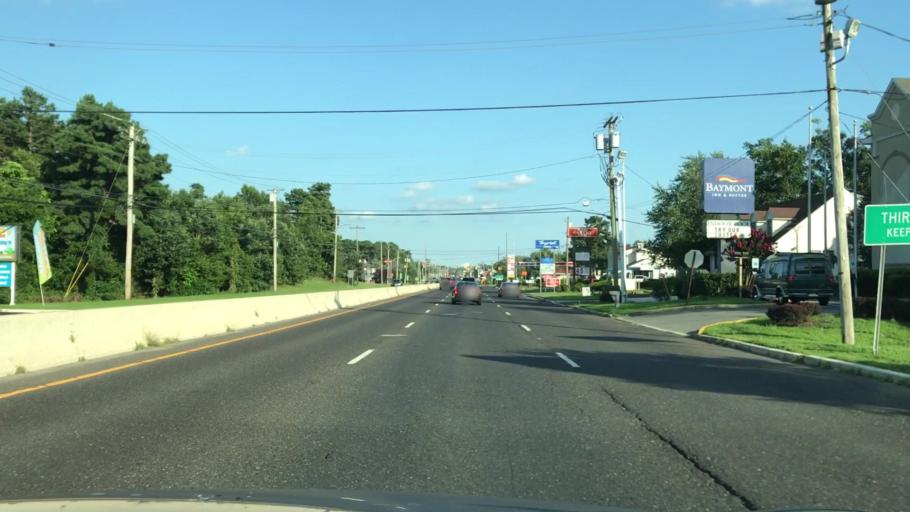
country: US
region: New Jersey
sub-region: Atlantic County
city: Absecon
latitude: 39.4505
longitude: -74.5350
